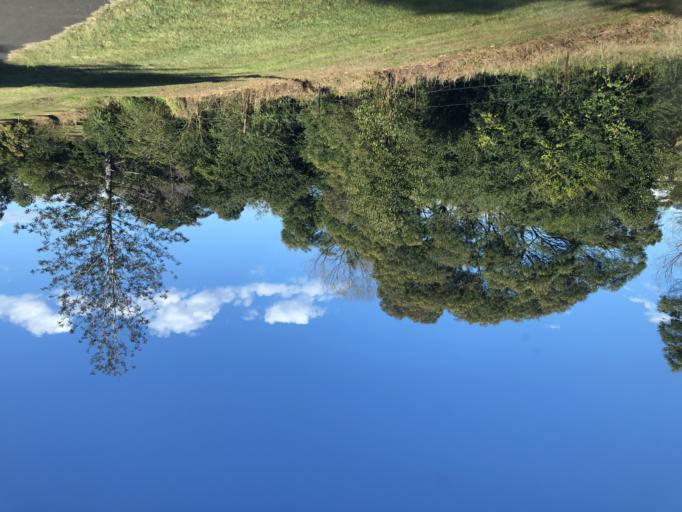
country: AU
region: New South Wales
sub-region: Nambucca Shire
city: Bowraville
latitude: -30.6495
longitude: 152.8571
